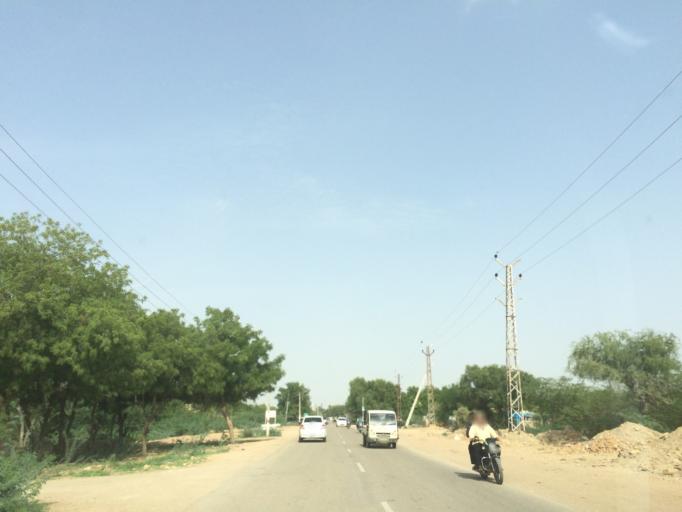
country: IN
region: Rajasthan
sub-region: Jaisalmer
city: Jaisalmer
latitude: 26.9115
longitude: 70.9250
